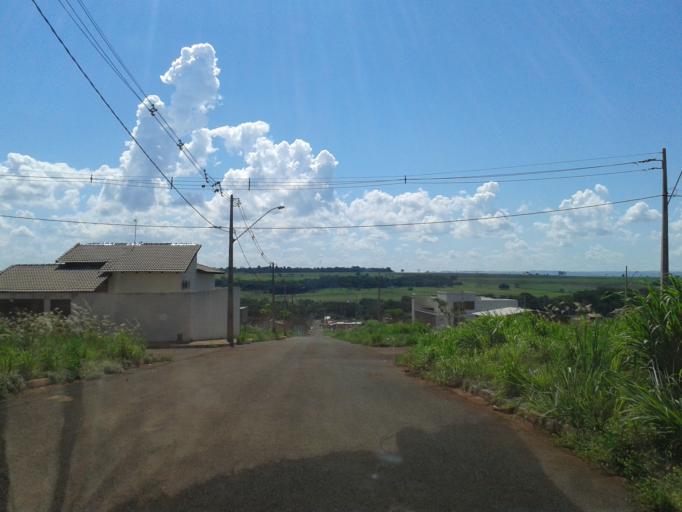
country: BR
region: Goias
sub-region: Itumbiara
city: Itumbiara
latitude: -18.4265
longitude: -49.1855
